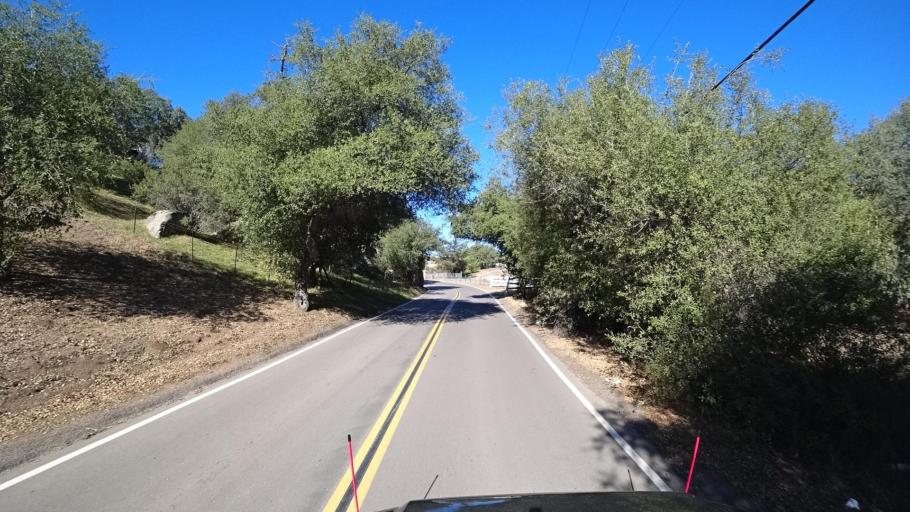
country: MX
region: Baja California
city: Tecate
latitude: 32.6749
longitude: -116.7127
